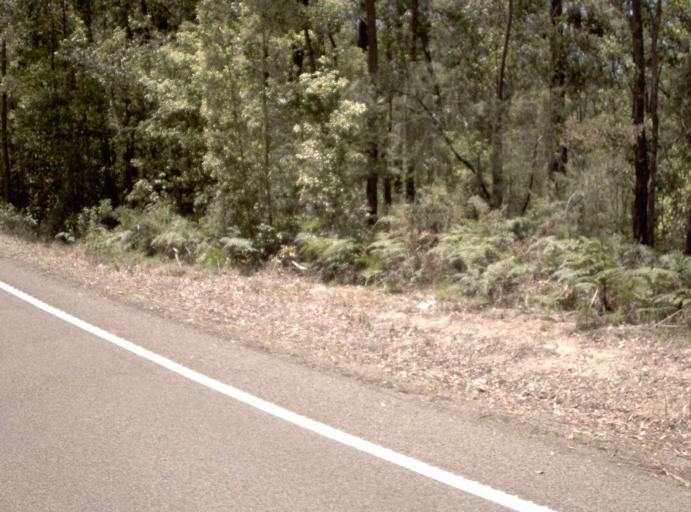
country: AU
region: Victoria
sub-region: East Gippsland
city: Lakes Entrance
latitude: -37.7647
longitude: 148.0586
